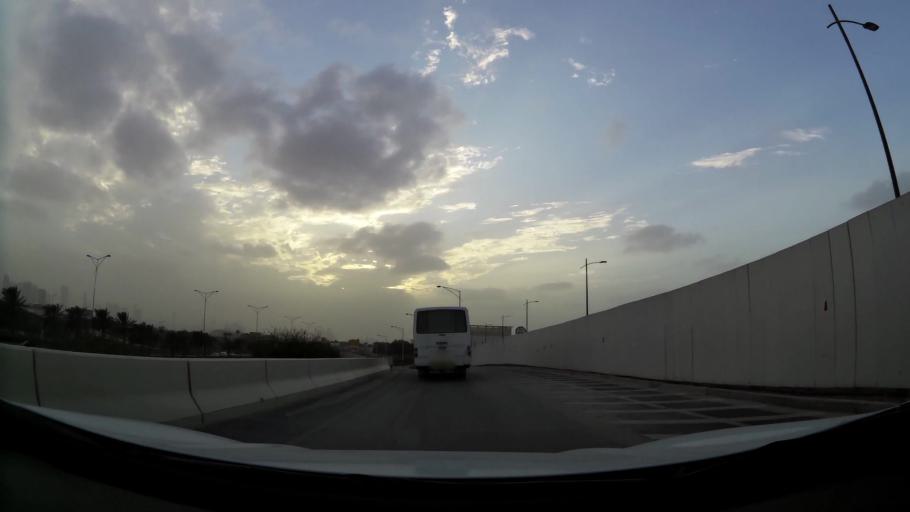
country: AE
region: Abu Dhabi
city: Abu Dhabi
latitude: 24.5315
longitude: 54.4184
